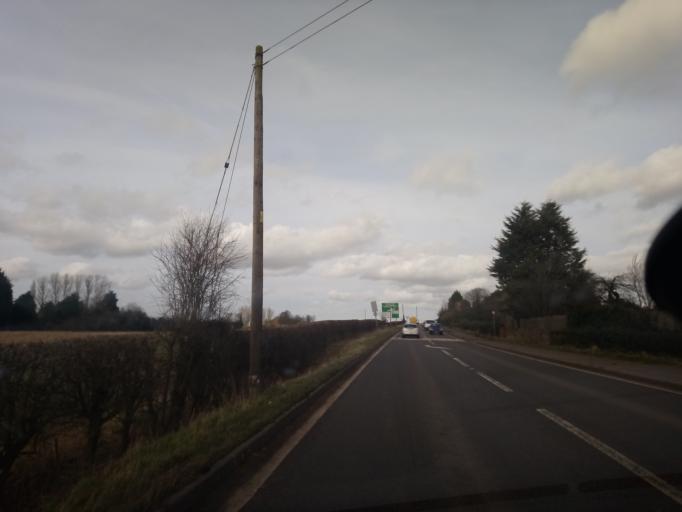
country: GB
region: England
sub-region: Telford and Wrekin
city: Eyton upon the Weald Moors
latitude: 52.7571
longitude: -2.5493
